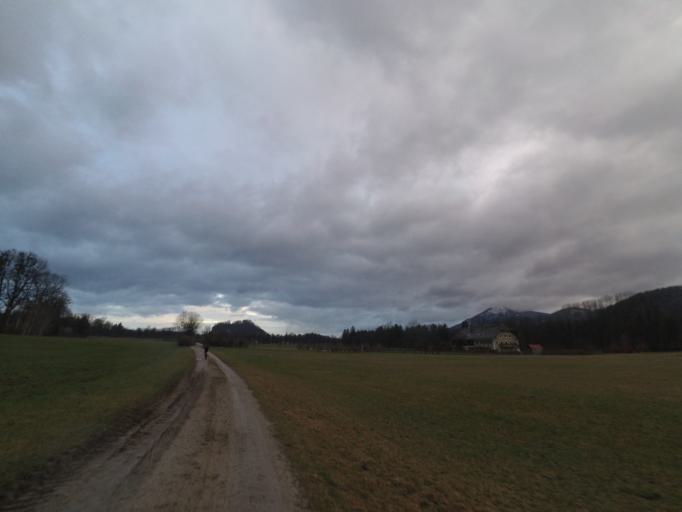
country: AT
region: Salzburg
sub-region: Politischer Bezirk Salzburg-Umgebung
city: Elsbethen
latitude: 47.7435
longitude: 13.0767
